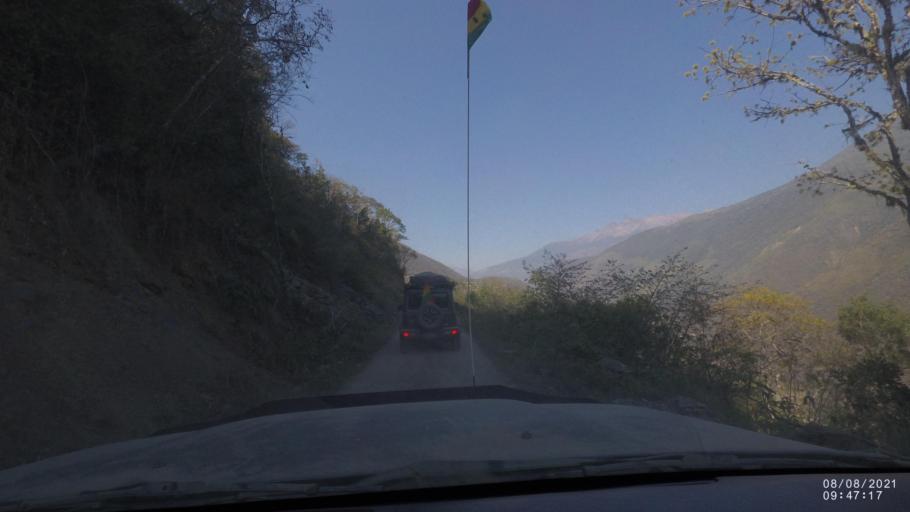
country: BO
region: La Paz
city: Quime
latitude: -16.6086
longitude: -66.7294
